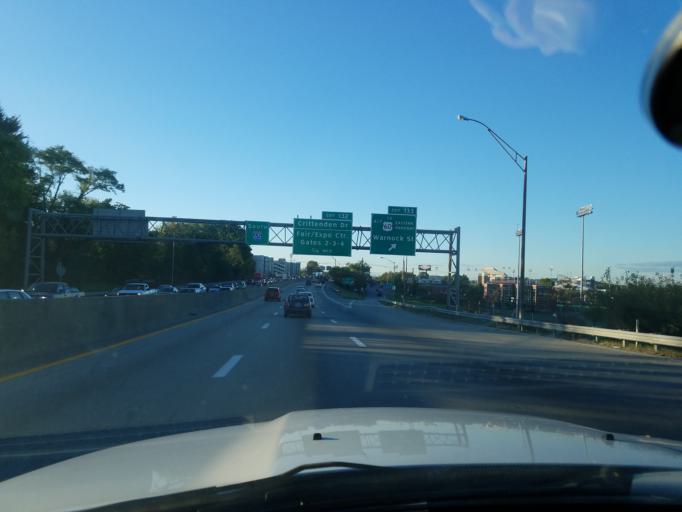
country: US
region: Kentucky
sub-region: Jefferson County
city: Audubon Park
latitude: 38.2175
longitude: -85.7523
